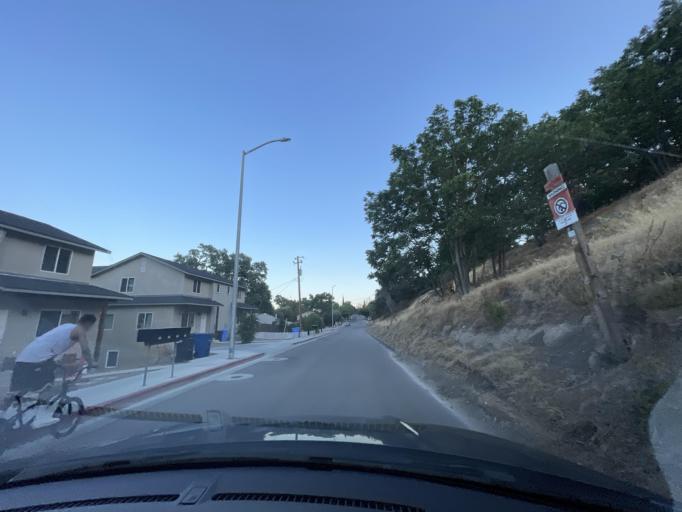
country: US
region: California
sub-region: San Luis Obispo County
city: Paso Robles
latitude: 35.6488
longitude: -120.6958
